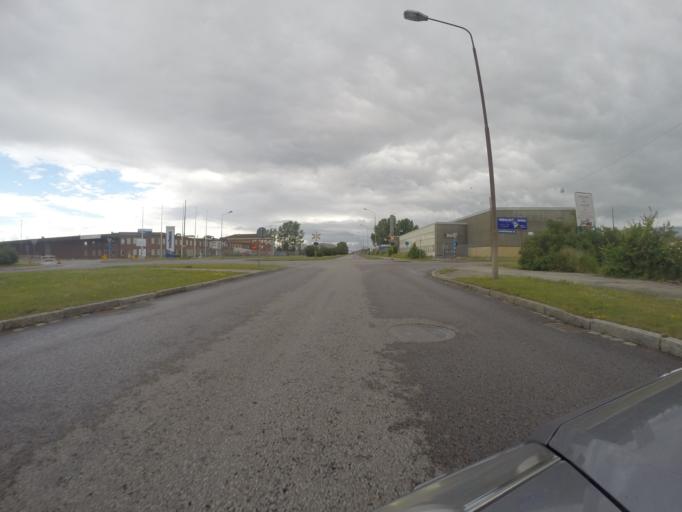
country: SE
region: Skane
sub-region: Burlovs Kommun
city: Arloev
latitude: 55.6278
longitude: 13.0369
